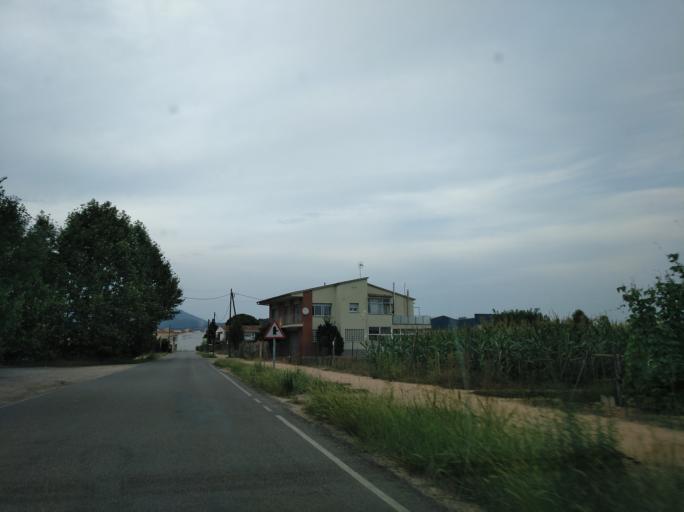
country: ES
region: Catalonia
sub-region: Provincia de Girona
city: Santa Coloma de Farners
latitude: 41.8531
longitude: 2.6715
